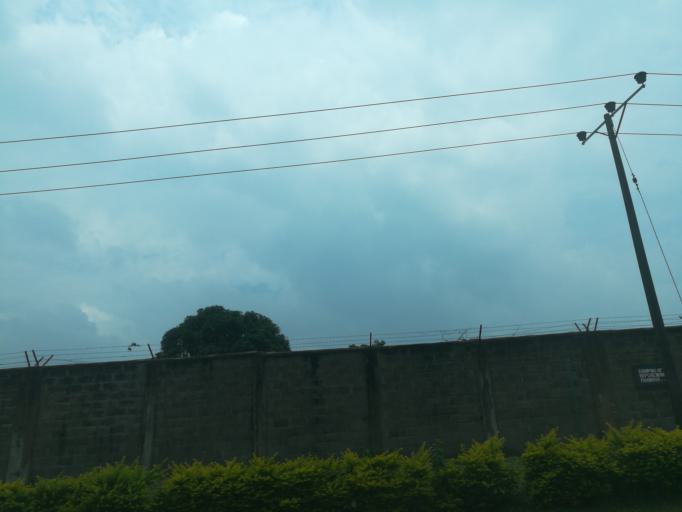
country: NG
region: Lagos
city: Ikorodu
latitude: 6.5639
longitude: 3.6003
